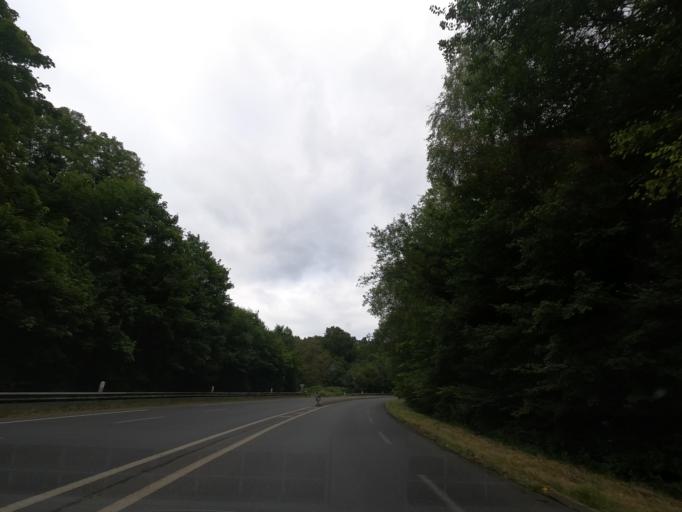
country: FR
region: Haute-Normandie
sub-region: Departement de la Seine-Maritime
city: Sahurs
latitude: 49.3383
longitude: 0.9209
